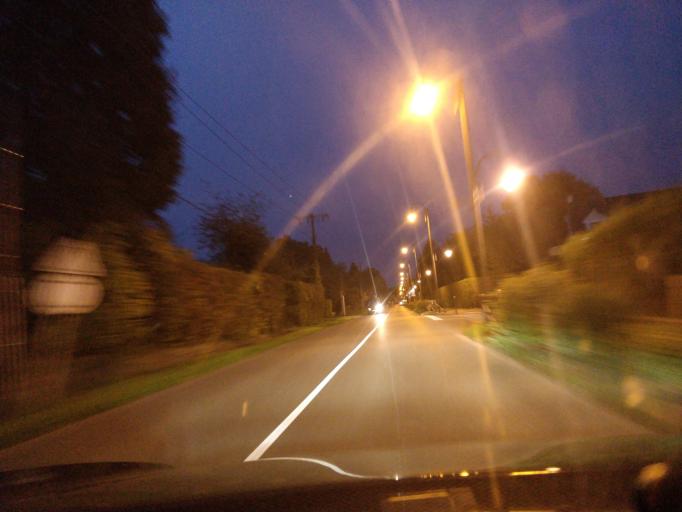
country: FR
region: Ile-de-France
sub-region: Departement de l'Essonne
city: Limours
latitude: 48.6296
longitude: 2.0843
